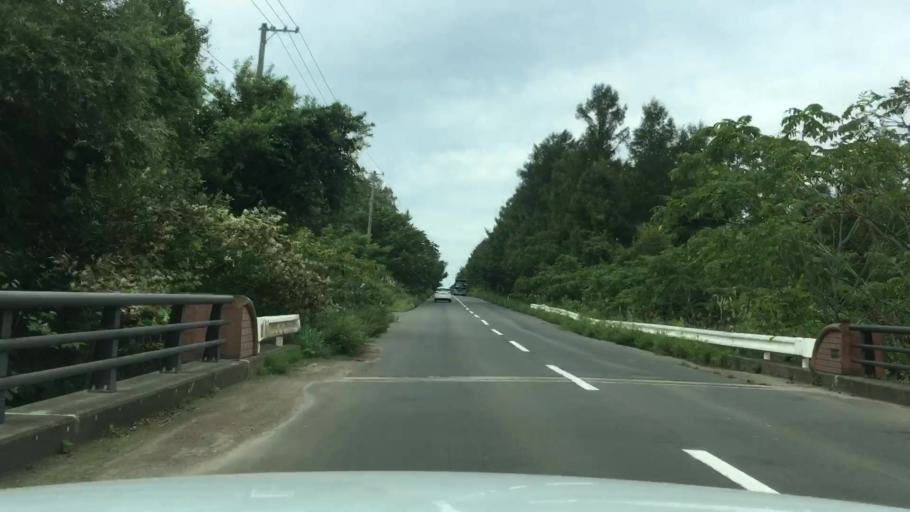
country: JP
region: Aomori
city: Shimokizukuri
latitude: 40.7116
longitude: 140.3296
